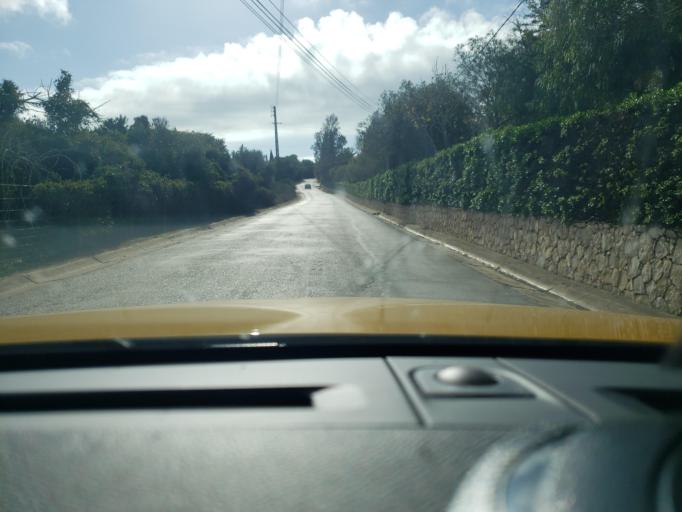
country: PT
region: Faro
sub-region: Lagoa
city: Carvoeiro
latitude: 37.1065
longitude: -8.4558
